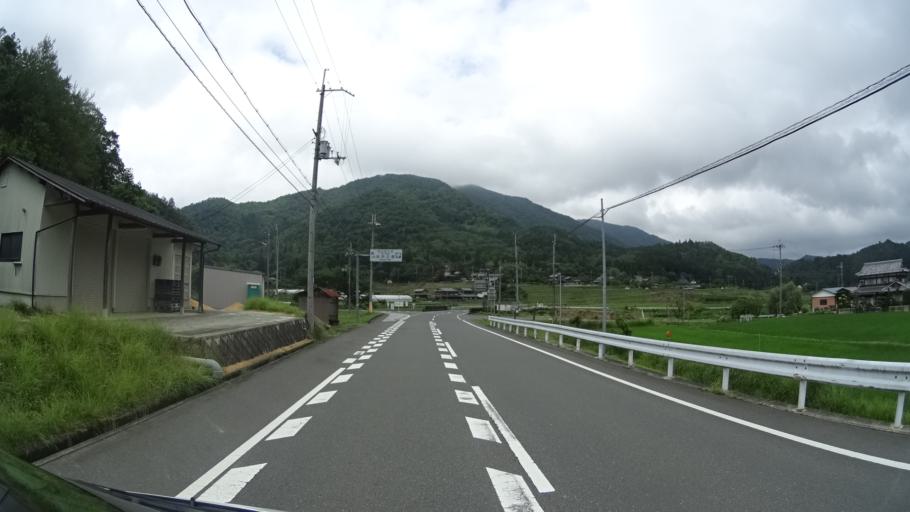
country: JP
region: Kyoto
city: Kameoka
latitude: 35.0498
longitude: 135.4159
